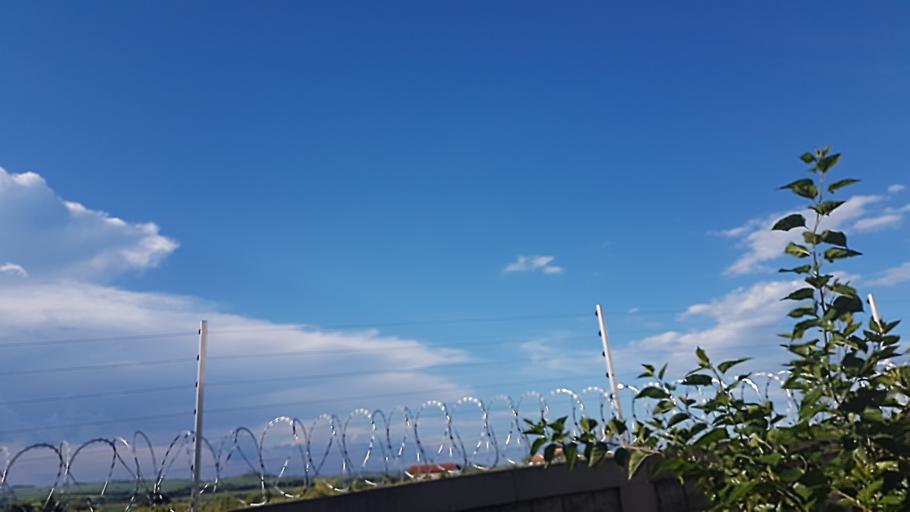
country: BR
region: Parana
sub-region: Ibipora
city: Ibipora
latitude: -23.2702
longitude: -51.0669
